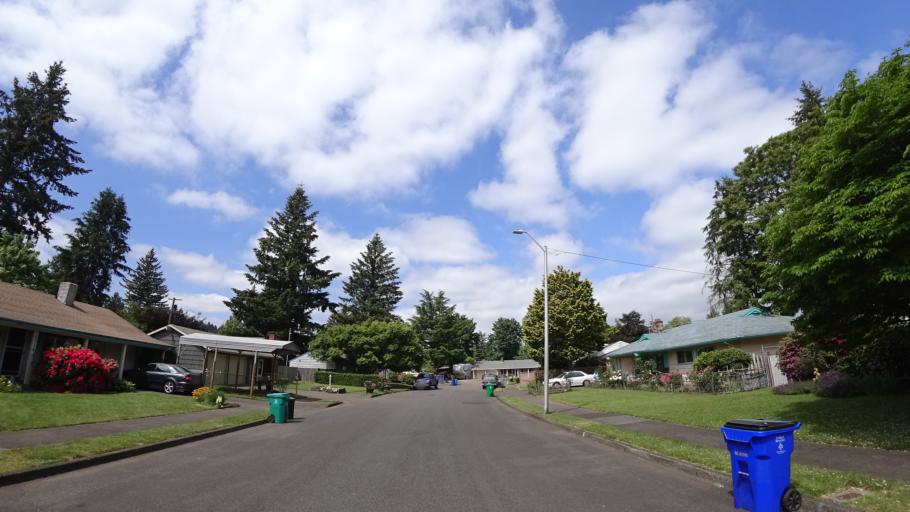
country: US
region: Oregon
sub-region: Multnomah County
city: Gresham
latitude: 45.4972
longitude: -122.4899
